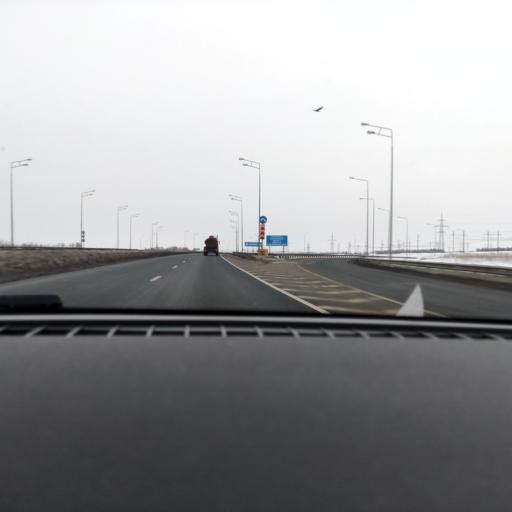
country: RU
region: Samara
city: Smyshlyayevka
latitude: 53.1320
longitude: 50.4244
